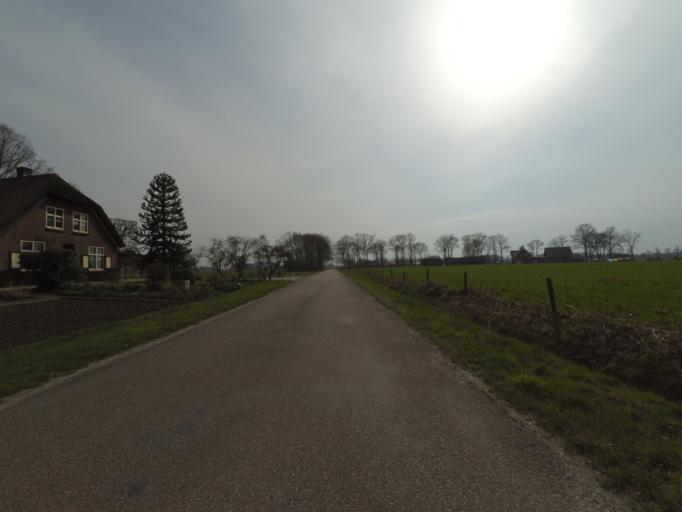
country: NL
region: Gelderland
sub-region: Gemeente Ede
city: Lunteren
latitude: 52.0962
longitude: 5.5897
